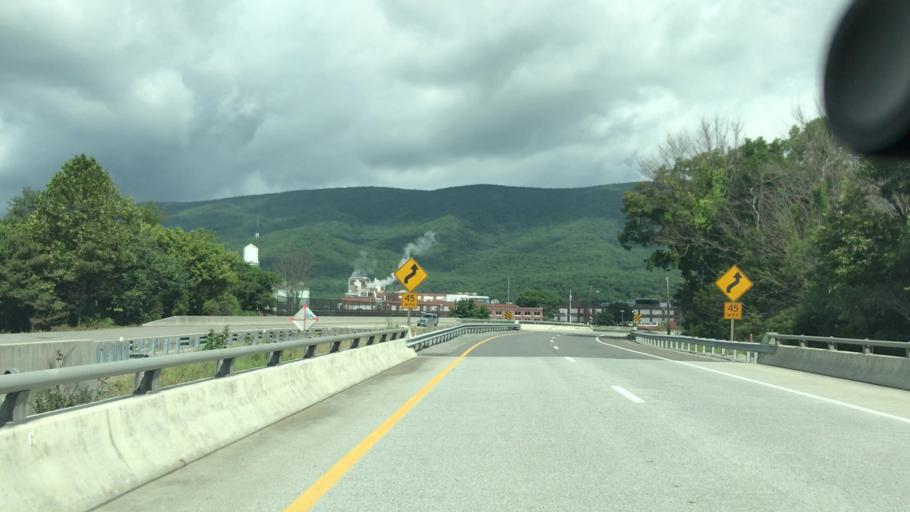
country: US
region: Virginia
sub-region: Giles County
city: Pearisburg
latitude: 37.3410
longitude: -80.7584
